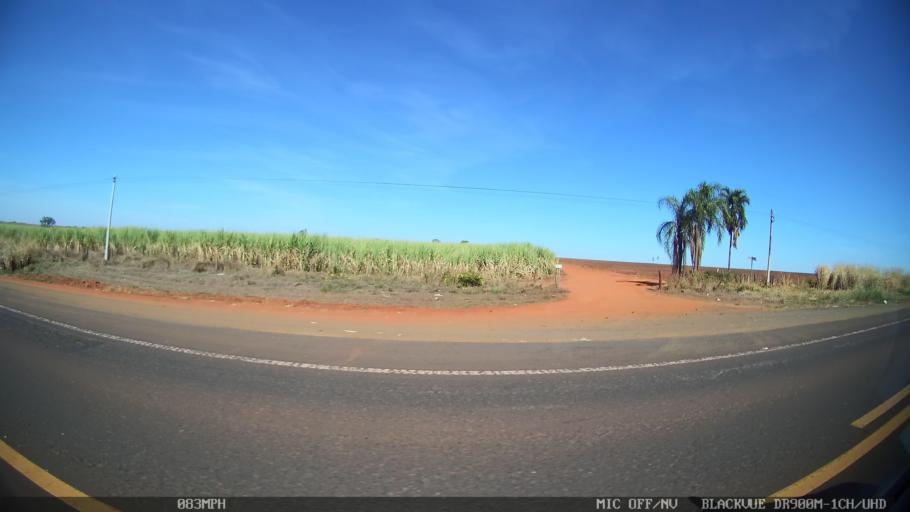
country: BR
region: Sao Paulo
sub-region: Barretos
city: Barretos
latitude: -20.5536
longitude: -48.6390
